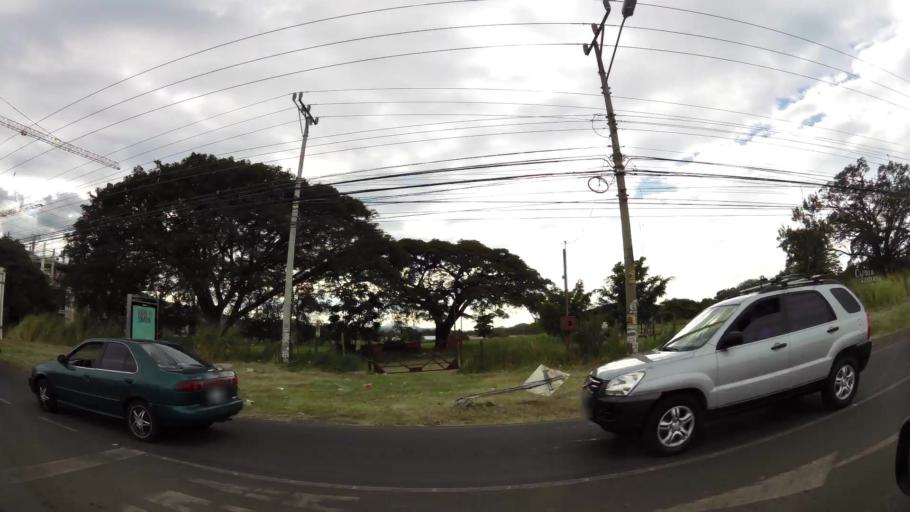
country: CR
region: Heredia
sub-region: Canton de Belen
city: San Antonio
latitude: 9.9588
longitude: -84.1965
